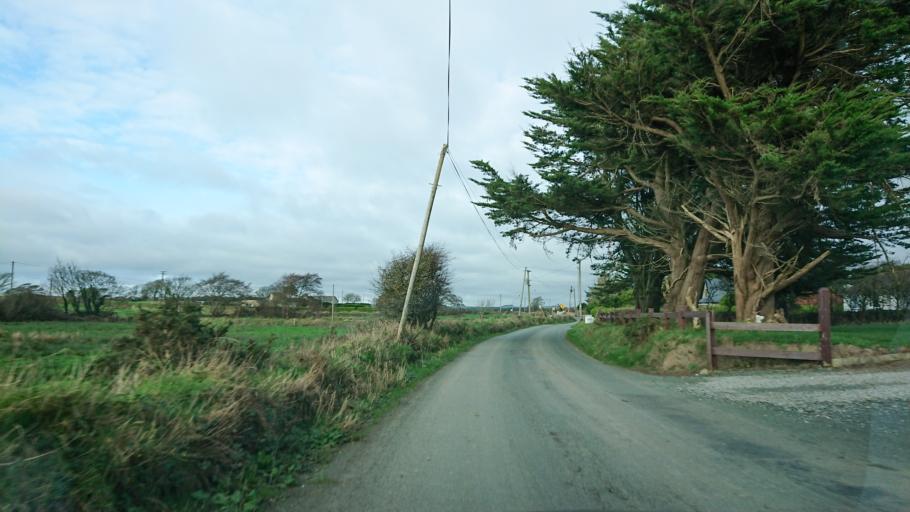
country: IE
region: Munster
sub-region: Waterford
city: Portlaw
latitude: 52.1491
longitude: -7.3090
